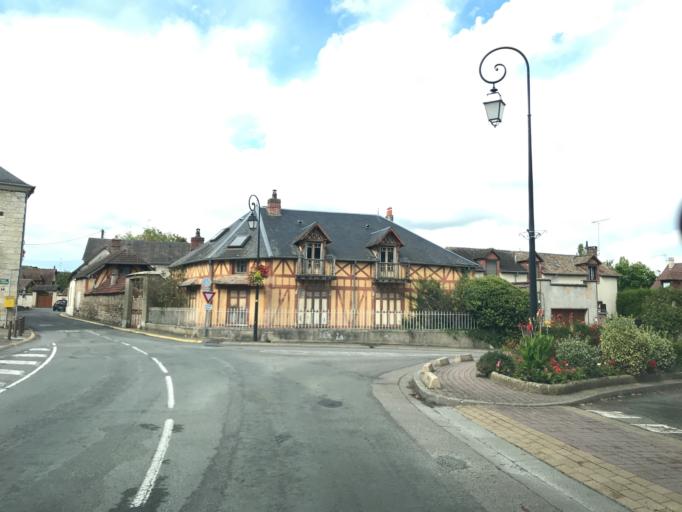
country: FR
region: Haute-Normandie
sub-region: Departement de l'Eure
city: Saint-Just
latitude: 49.1084
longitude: 1.4405
